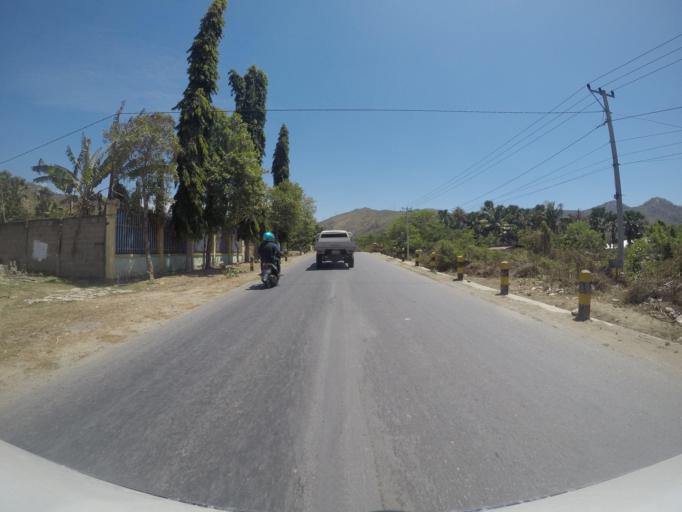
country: TL
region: Dili
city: Dili
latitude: -8.5557
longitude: 125.6533
